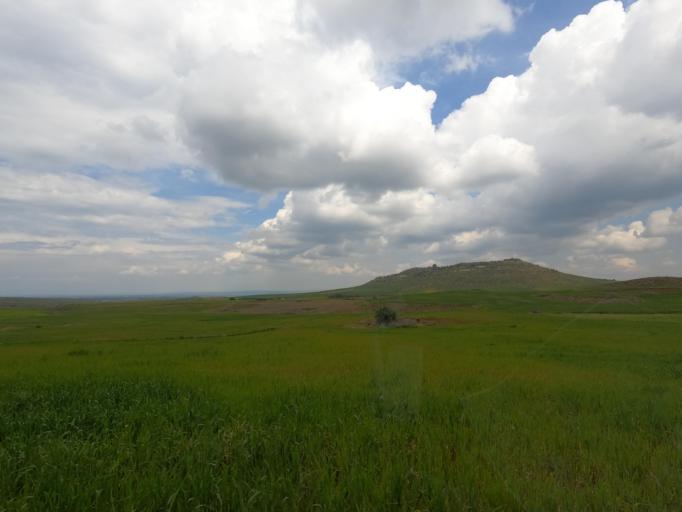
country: CY
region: Lefkosia
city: Lefka
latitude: 35.0851
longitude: 32.9476
